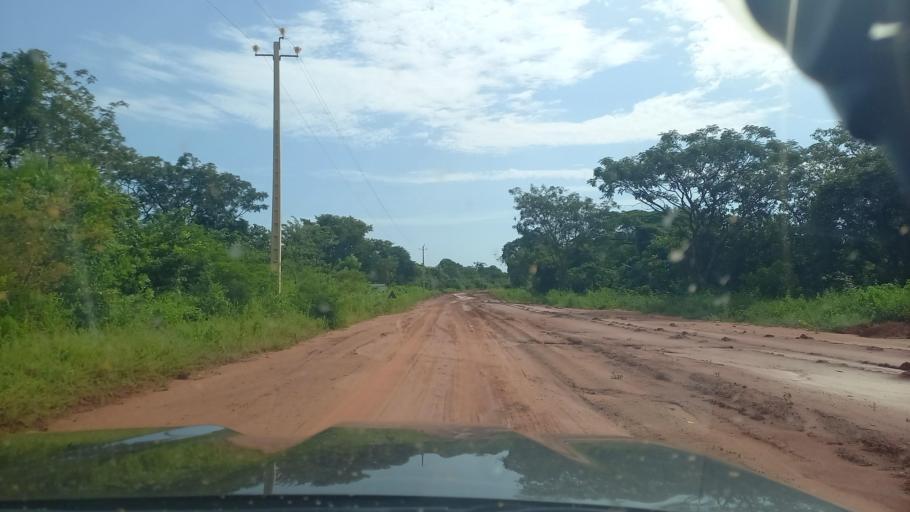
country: SN
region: Ziguinchor
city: Ziguinchor
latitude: 12.6712
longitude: -16.2196
